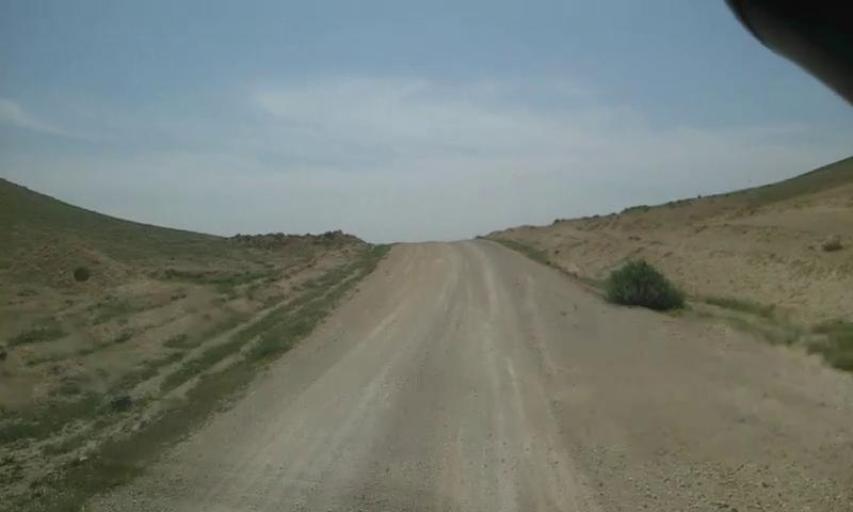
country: PS
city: `Arab ar Rashaydah
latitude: 31.4960
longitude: 35.2935
